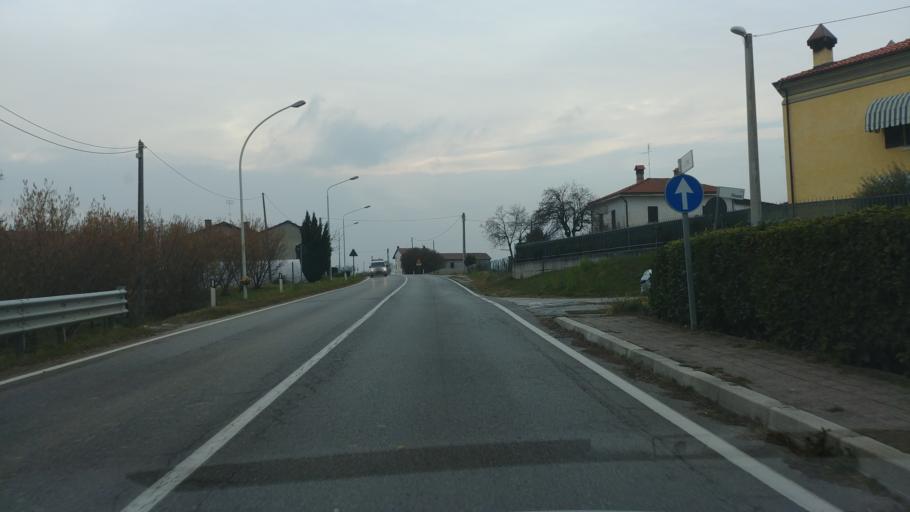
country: IT
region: Piedmont
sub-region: Provincia di Cuneo
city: Castelletto Stura
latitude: 44.4330
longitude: 7.5862
